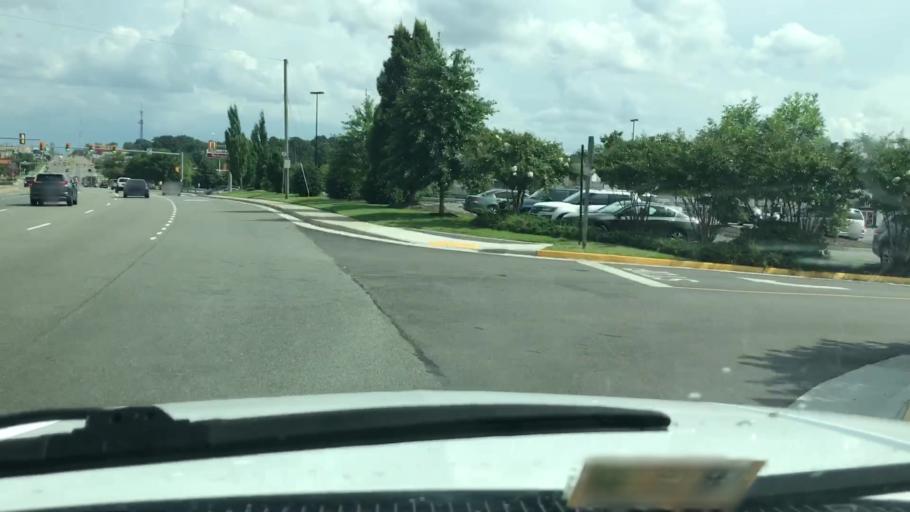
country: US
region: Virginia
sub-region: Henrico County
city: Dumbarton
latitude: 37.5984
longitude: -77.5140
